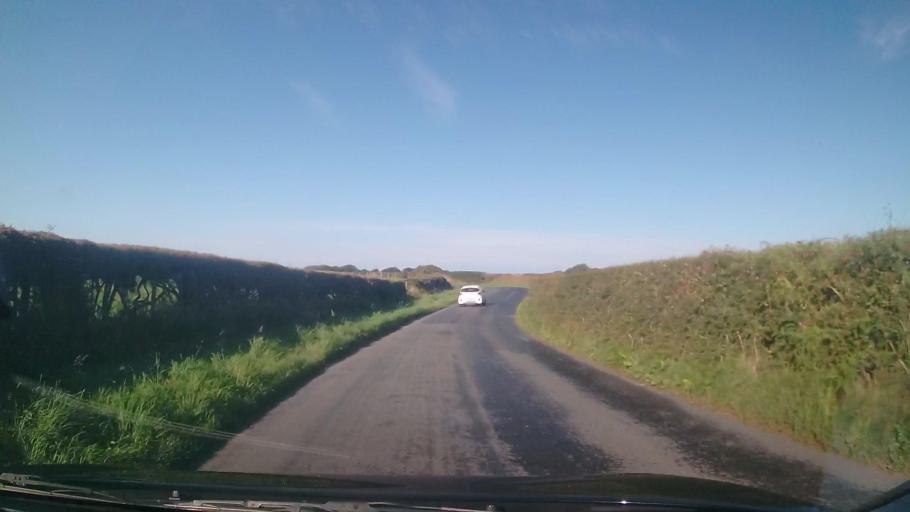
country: GB
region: England
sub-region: Cumbria
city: Seascale
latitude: 54.3825
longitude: -3.4103
